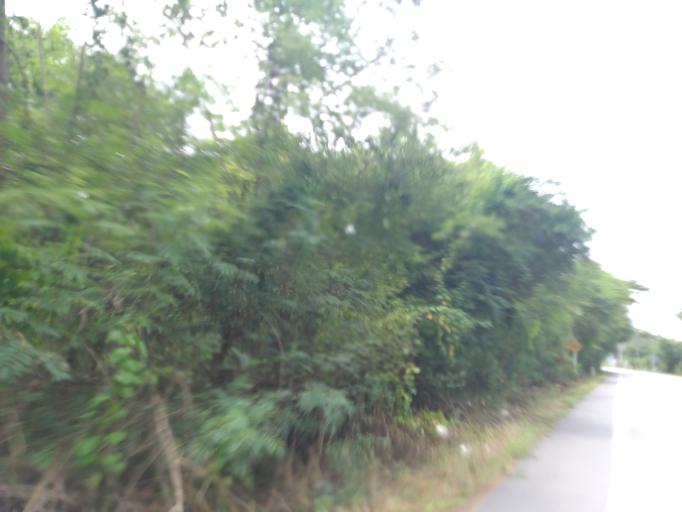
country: TH
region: Pathum Thani
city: Nong Suea
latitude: 14.0670
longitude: 100.8717
